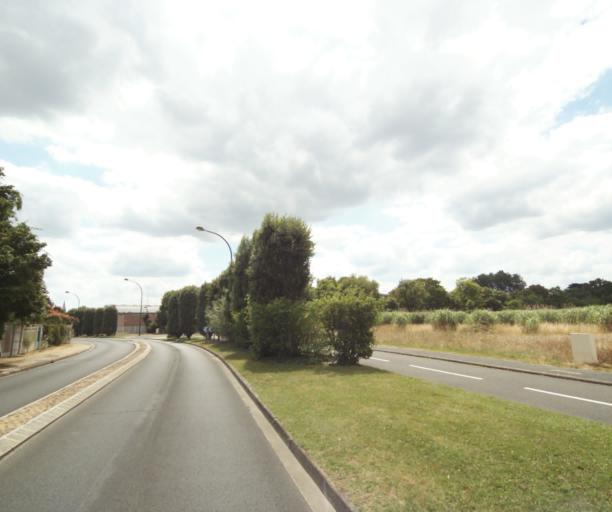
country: FR
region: Centre
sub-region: Departement du Loiret
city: Saint-Cyr-en-Val
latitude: 47.8336
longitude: 1.9629
